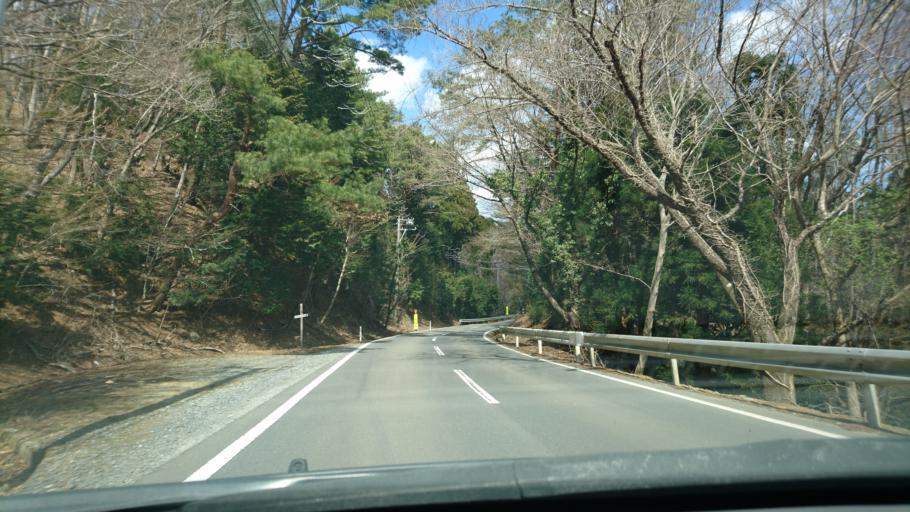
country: JP
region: Miyagi
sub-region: Oshika Gun
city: Onagawa Cho
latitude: 38.4743
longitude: 141.4913
